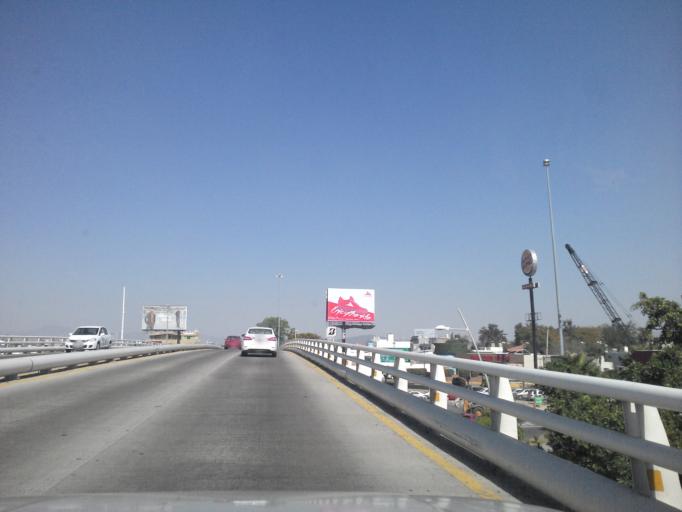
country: MX
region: Jalisco
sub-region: Zapopan
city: Zapopan
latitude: 20.7045
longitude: -103.3645
